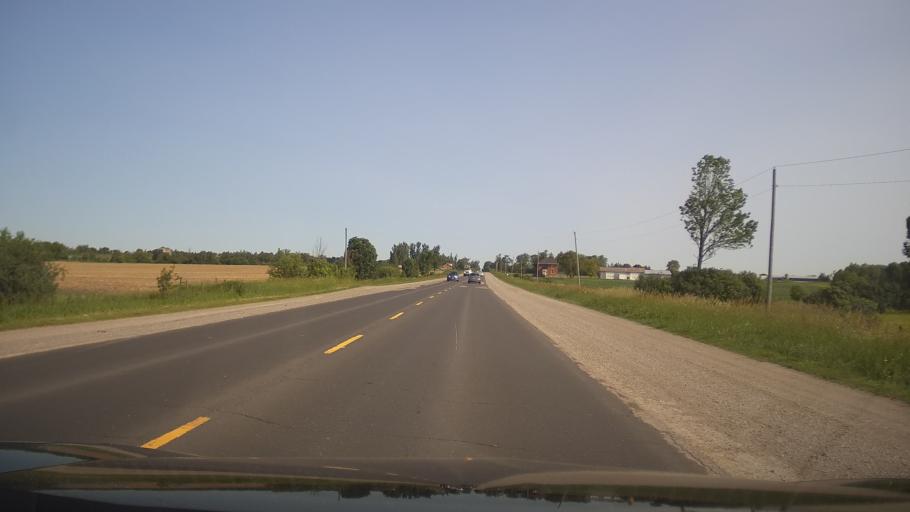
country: CA
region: Ontario
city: Omemee
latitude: 44.3255
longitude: -78.6851
